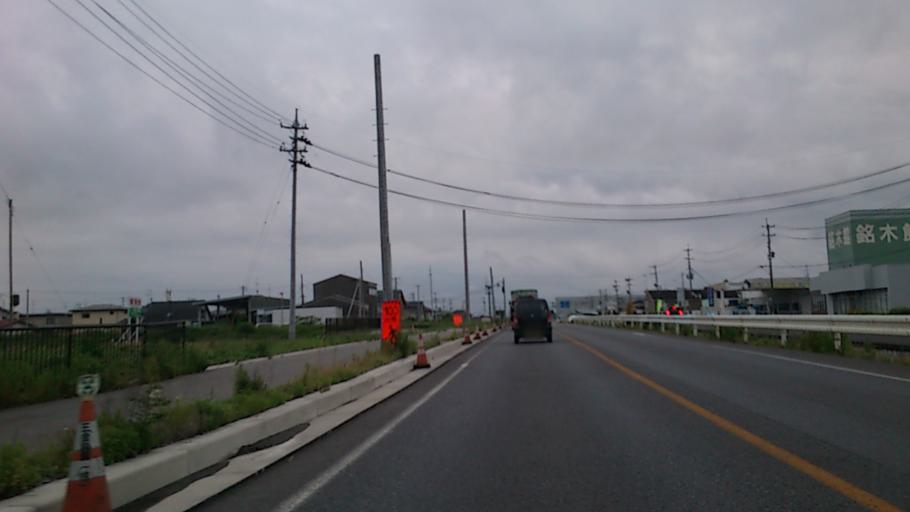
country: JP
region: Fukushima
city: Sukagawa
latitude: 37.2584
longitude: 140.3465
